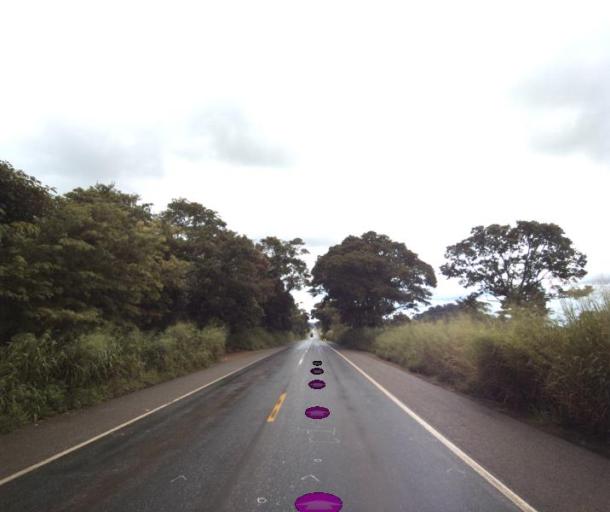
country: BR
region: Goias
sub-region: Pirenopolis
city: Pirenopolis
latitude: -16.0611
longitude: -49.0648
